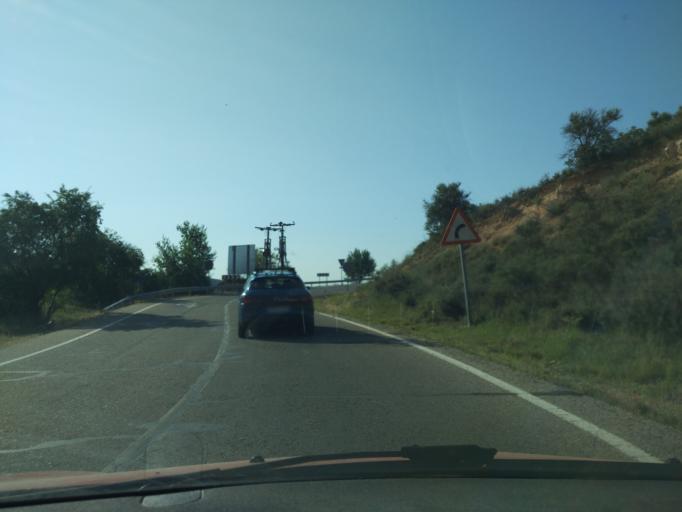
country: ES
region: Madrid
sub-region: Provincia de Madrid
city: Villar del Olmo
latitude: 40.3421
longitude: -3.2414
